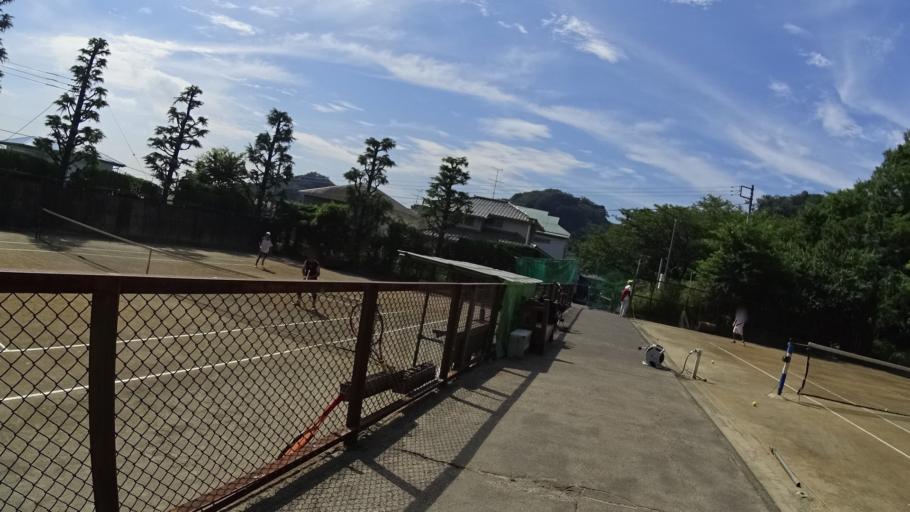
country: JP
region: Kanagawa
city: Zushi
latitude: 35.3092
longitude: 139.6126
